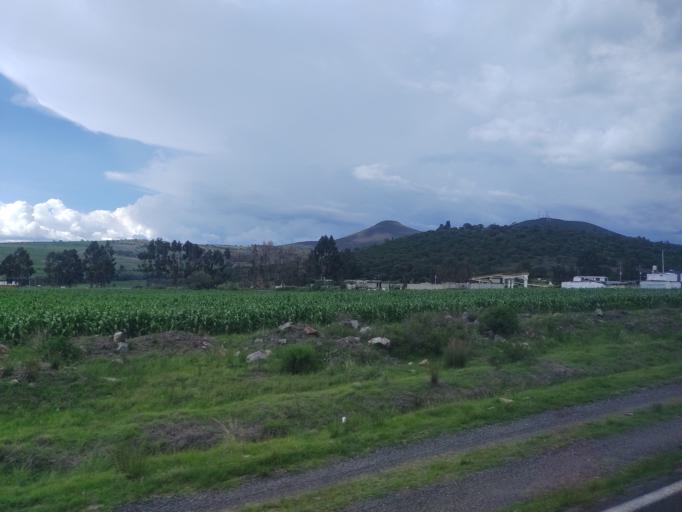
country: MX
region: Mexico
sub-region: Aculco
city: El Colorado
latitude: 20.1025
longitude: -99.7002
